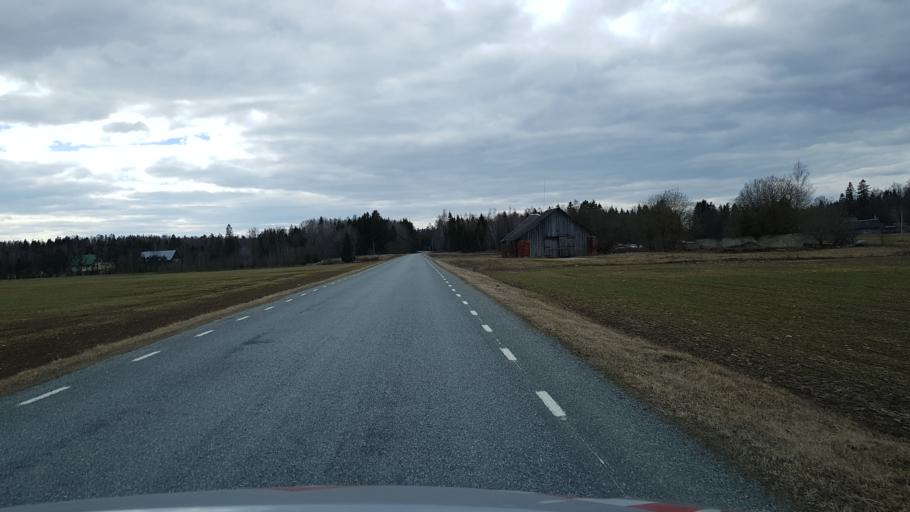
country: EE
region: Laeaene-Virumaa
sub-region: Kadrina vald
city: Kadrina
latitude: 59.2598
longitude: 26.2419
